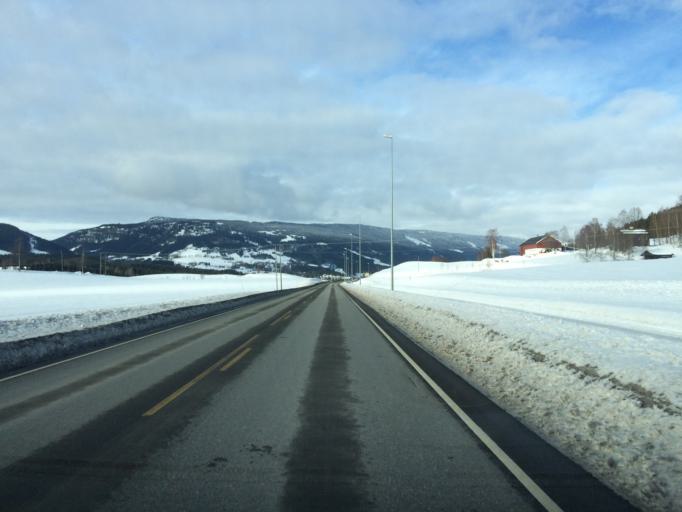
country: NO
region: Oppland
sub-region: Gausdal
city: Segalstad bru
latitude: 61.2206
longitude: 10.2473
